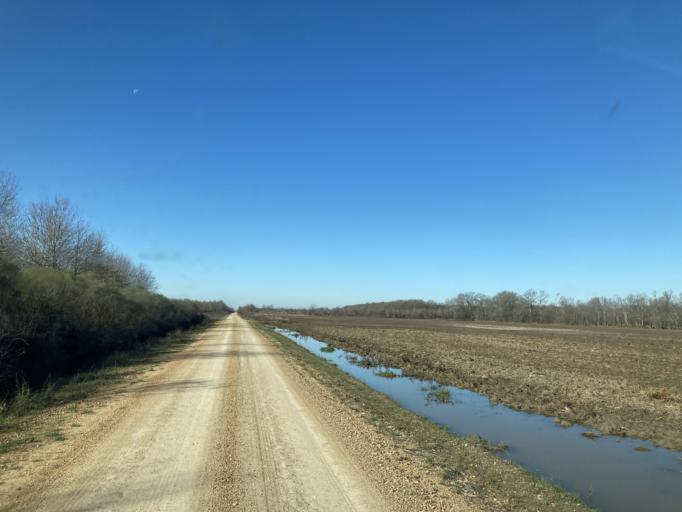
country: US
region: Mississippi
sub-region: Yazoo County
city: Yazoo City
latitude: 32.9518
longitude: -90.6173
